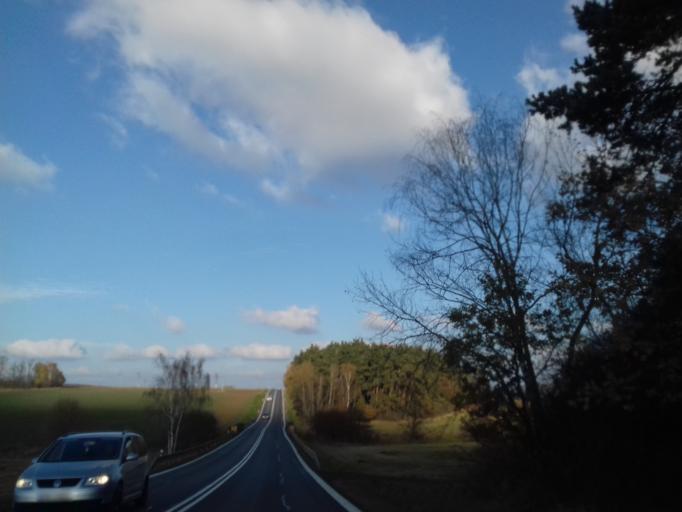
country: CZ
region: Plzensky
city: Holysov
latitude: 49.5841
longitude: 13.0838
